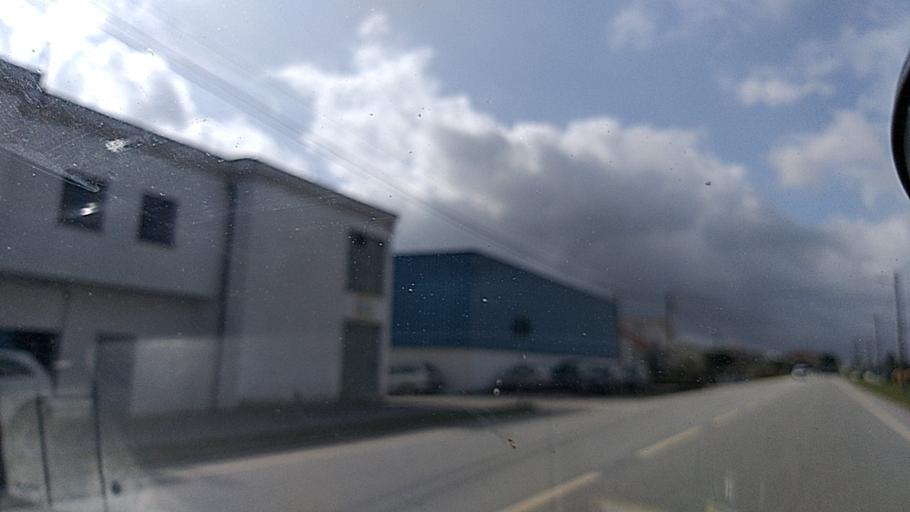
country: PT
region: Viseu
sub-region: Mangualde
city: Mangualde
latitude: 40.6656
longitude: -7.7136
